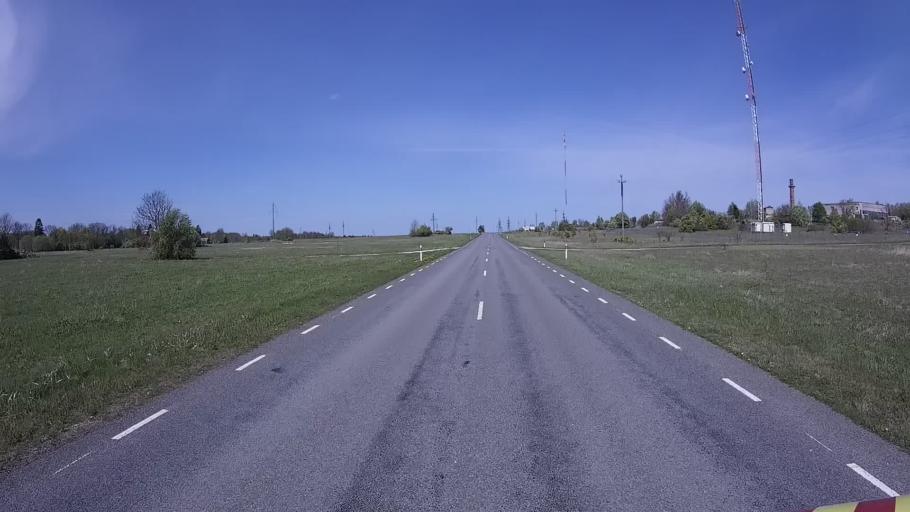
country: EE
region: Laeaene
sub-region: Lihula vald
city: Lihula
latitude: 58.6729
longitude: 23.8237
